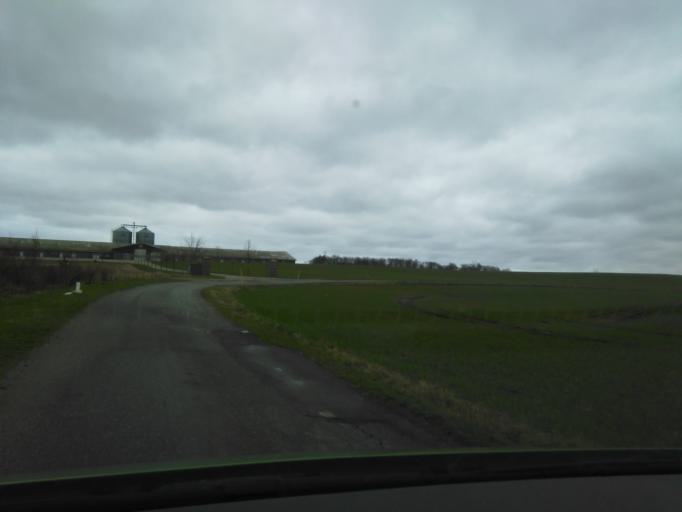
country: DK
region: Central Jutland
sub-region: Arhus Kommune
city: Solbjerg
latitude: 56.0411
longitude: 10.1240
